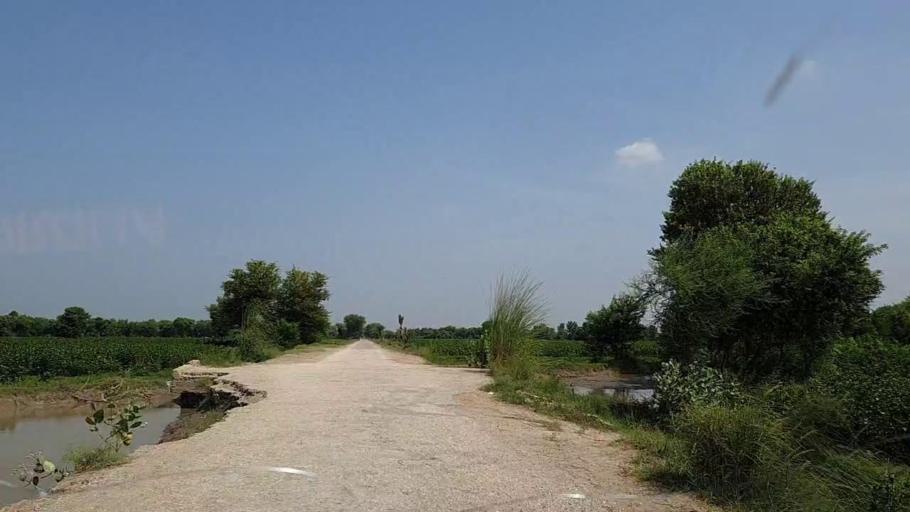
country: PK
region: Sindh
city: Adilpur
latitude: 27.8320
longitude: 69.2897
